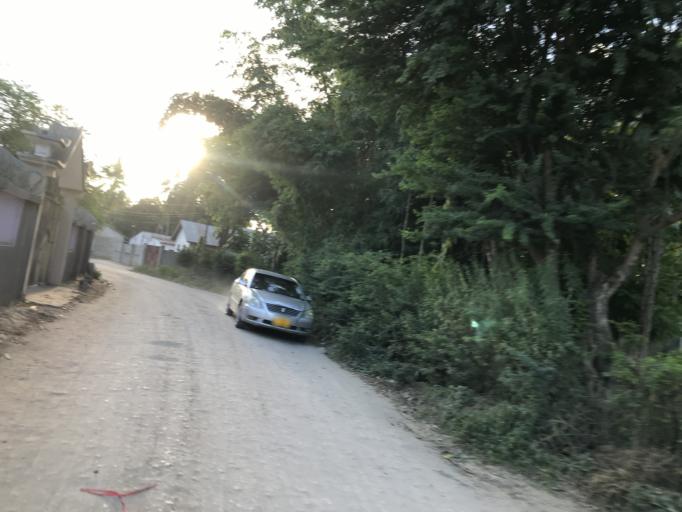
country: TZ
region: Dar es Salaam
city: Dar es Salaam
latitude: -6.8635
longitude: 39.3552
